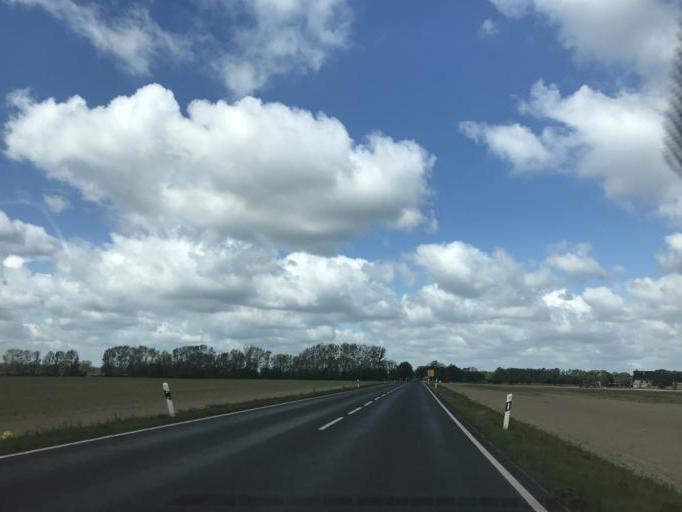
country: DE
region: Brandenburg
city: Liebenwalde
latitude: 52.8739
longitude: 13.4389
